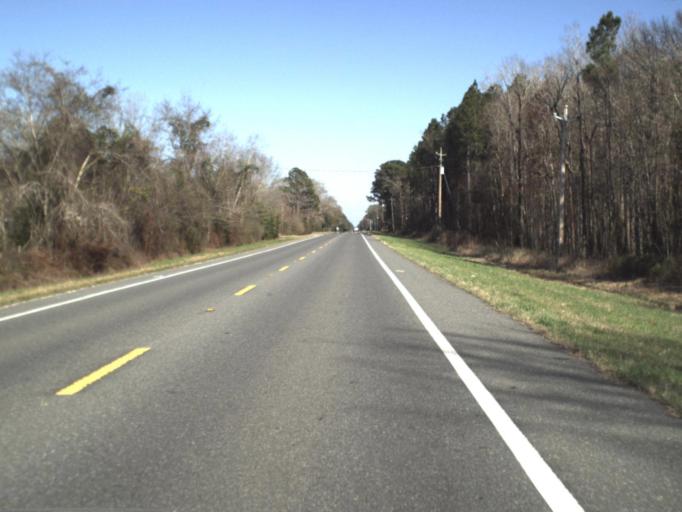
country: US
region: Florida
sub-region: Washington County
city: Chipley
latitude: 30.7867
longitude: -85.4435
